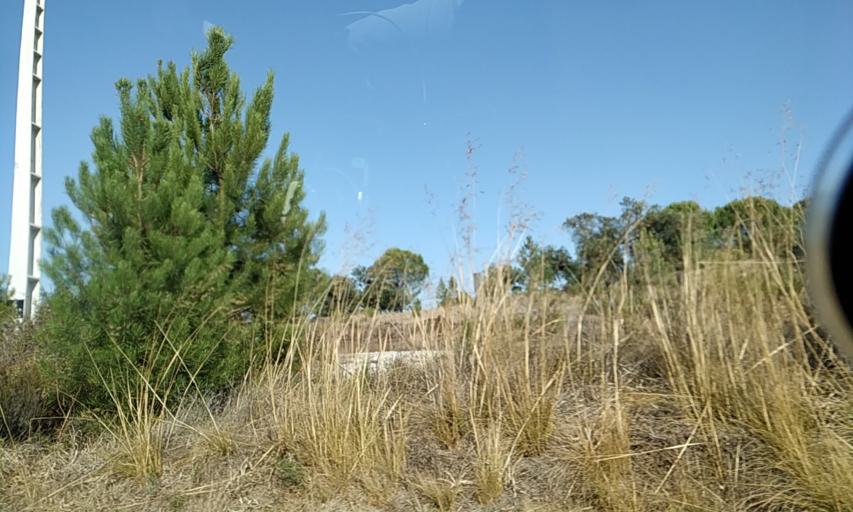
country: PT
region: Santarem
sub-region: Coruche
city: Coruche
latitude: 38.8830
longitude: -8.5388
